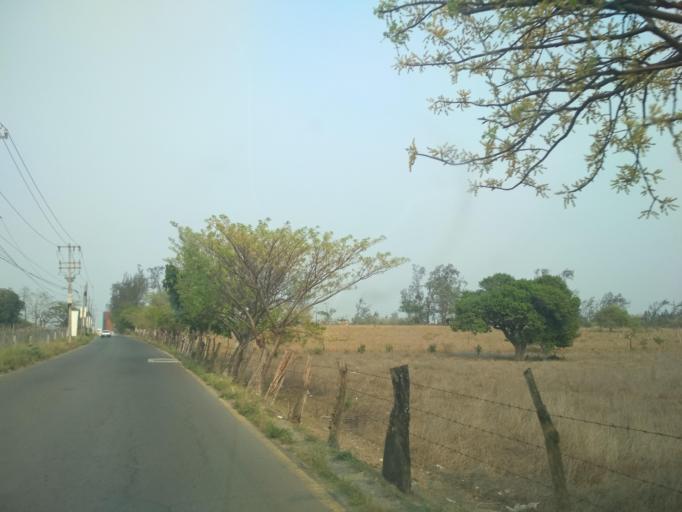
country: MX
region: Veracruz
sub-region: Veracruz
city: Las Amapolas
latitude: 19.1591
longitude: -96.1987
